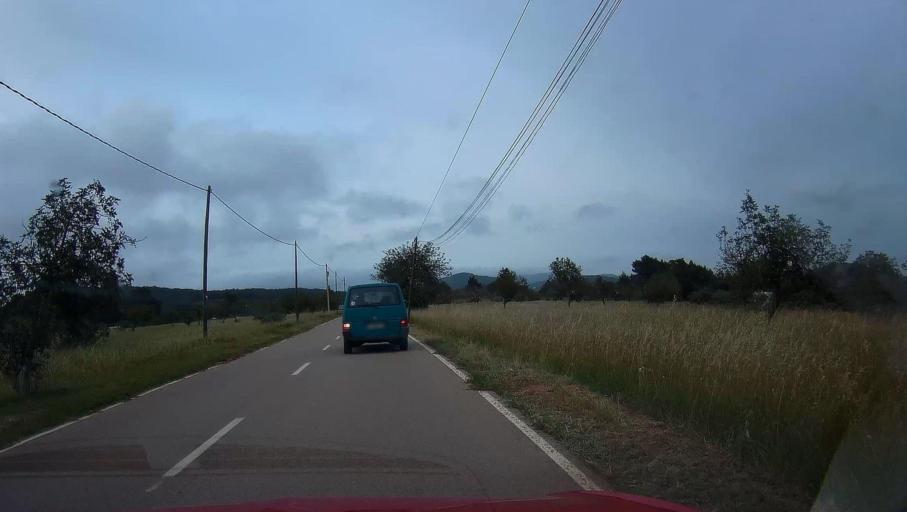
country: ES
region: Balearic Islands
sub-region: Illes Balears
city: Sant Joan de Labritja
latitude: 39.0465
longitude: 1.4159
